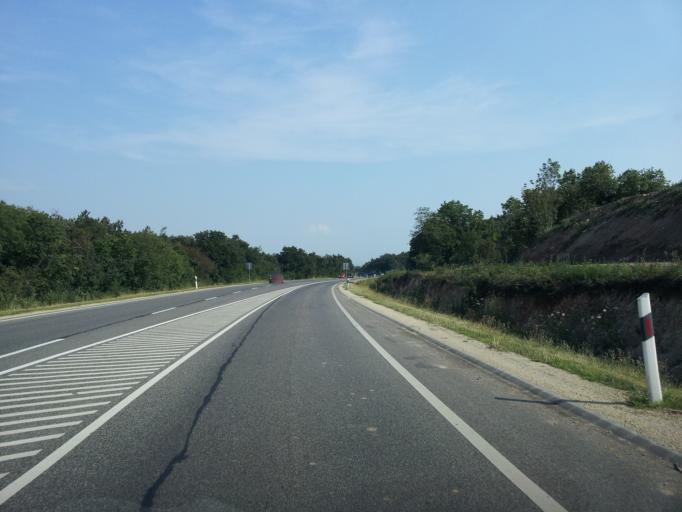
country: HU
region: Veszprem
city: Liter
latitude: 47.0929
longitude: 18.0254
